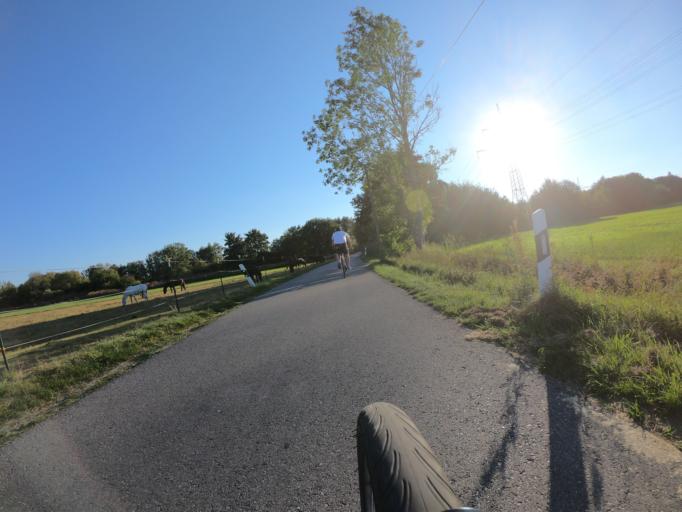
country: DE
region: Bavaria
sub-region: Upper Bavaria
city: Grobenzell
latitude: 48.1788
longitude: 11.3874
